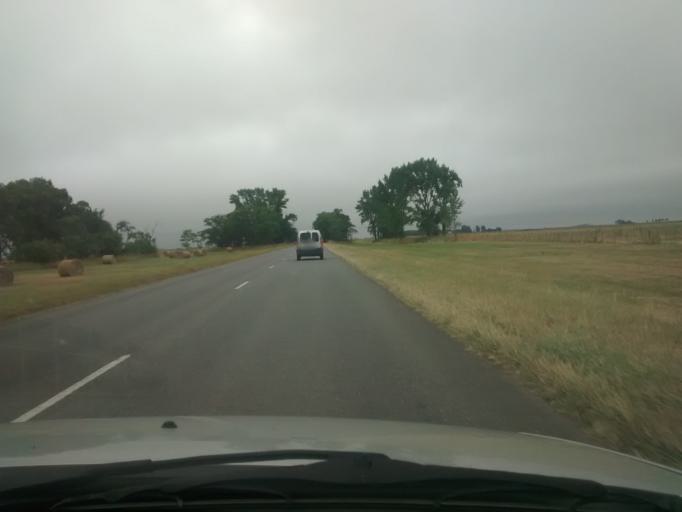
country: AR
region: Buenos Aires
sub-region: Partido de Ayacucho
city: Ayacucho
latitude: -37.2480
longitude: -58.4874
